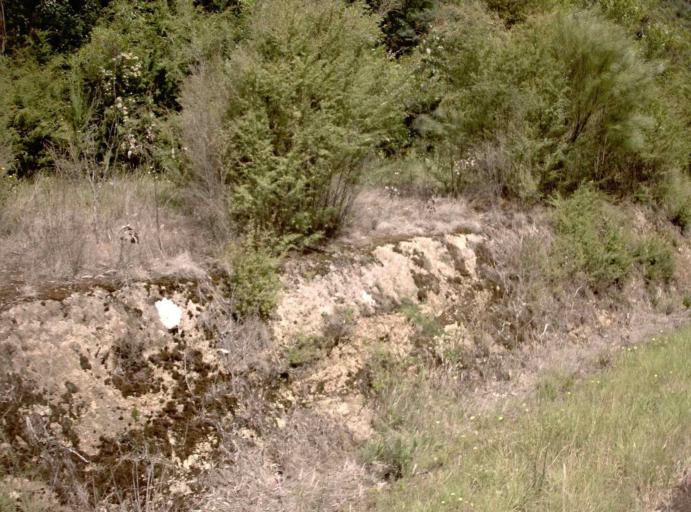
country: AU
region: Victoria
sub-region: Latrobe
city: Moe
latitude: -37.9083
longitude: 146.3956
